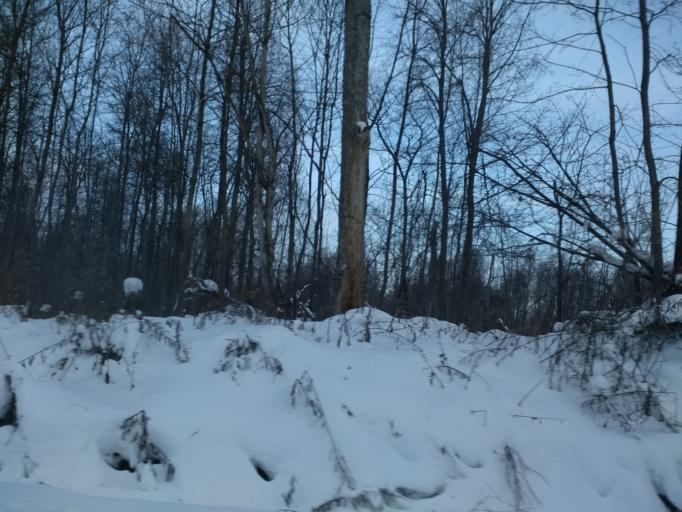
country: RU
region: Bashkortostan
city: Kudeyevskiy
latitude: 54.7131
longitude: 56.6392
